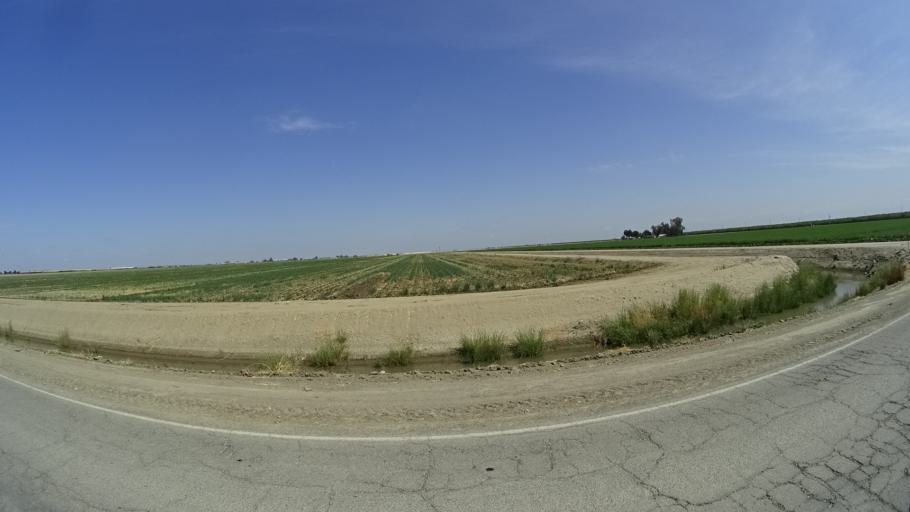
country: US
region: California
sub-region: Kings County
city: Home Garden
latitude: 36.2692
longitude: -119.5155
